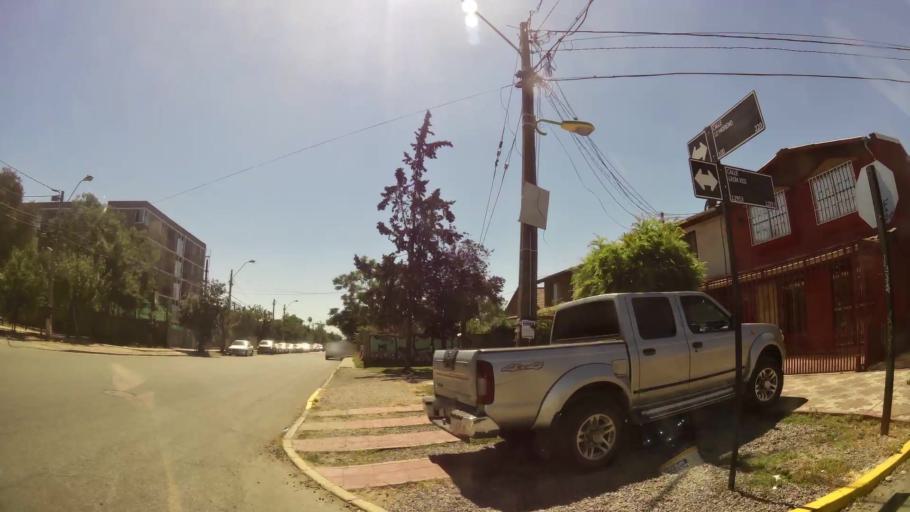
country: CL
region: Santiago Metropolitan
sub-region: Provincia de Maipo
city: San Bernardo
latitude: -33.5753
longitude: -70.6871
